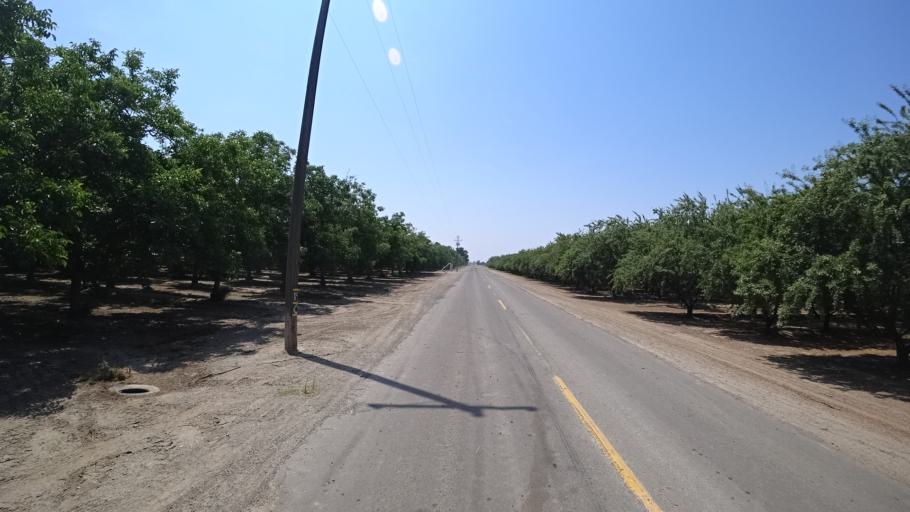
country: US
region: California
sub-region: Kings County
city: Lemoore
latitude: 36.3689
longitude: -119.7631
